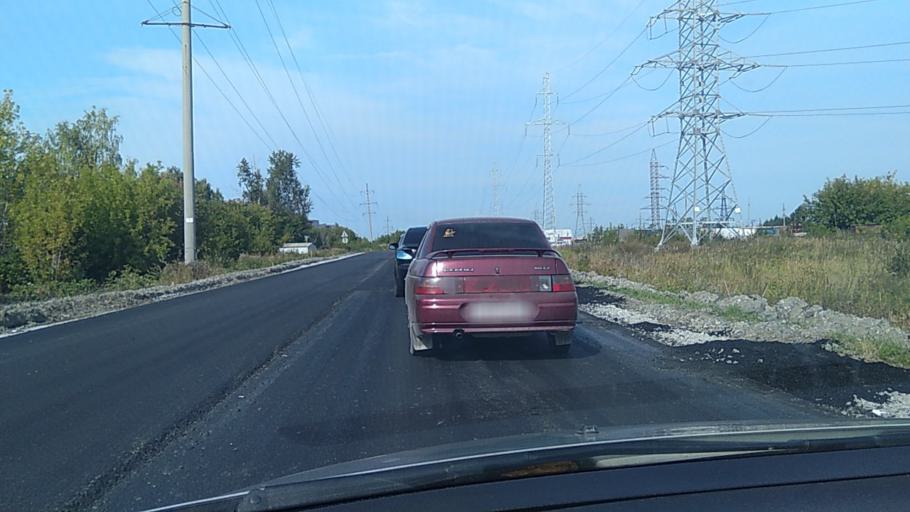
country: RU
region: Sverdlovsk
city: Sredneuralsk
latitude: 56.9869
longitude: 60.4778
